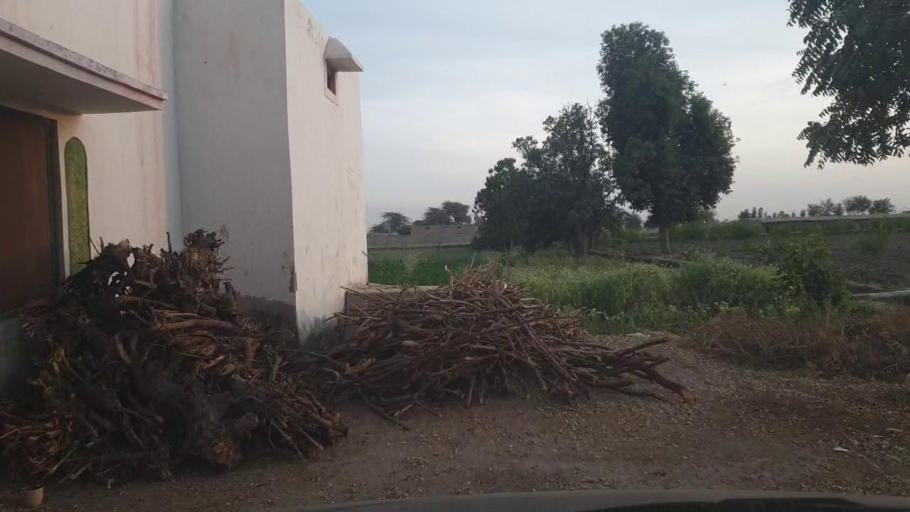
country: PK
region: Sindh
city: Kunri
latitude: 25.2246
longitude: 69.5651
